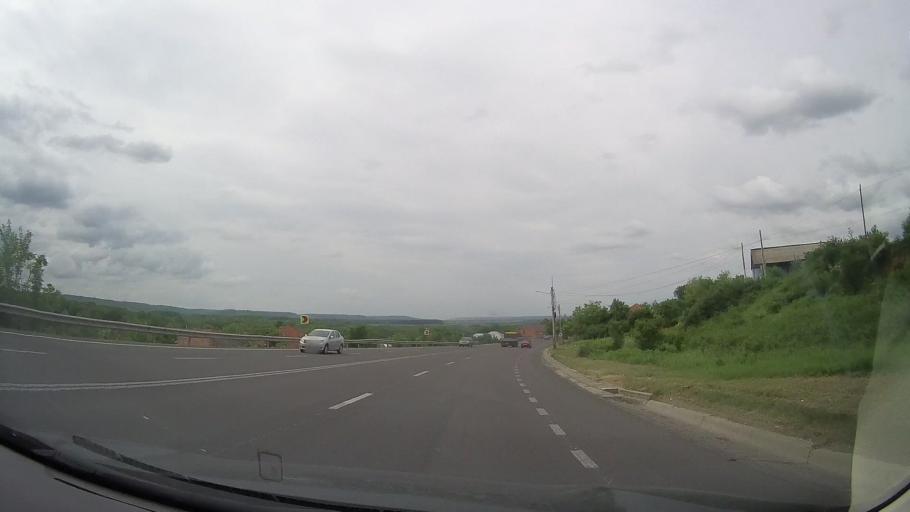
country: RO
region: Dolj
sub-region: Comuna Scaesti
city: Scaesti
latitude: 44.5014
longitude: 23.5980
